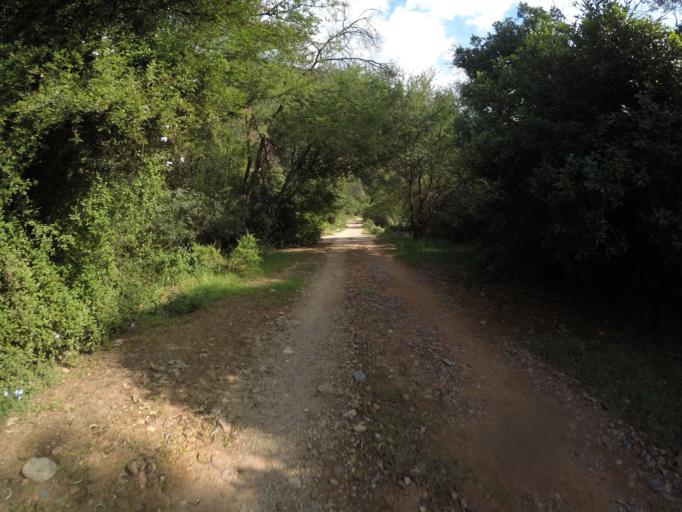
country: ZA
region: Eastern Cape
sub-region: Cacadu District Municipality
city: Kareedouw
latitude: -33.6424
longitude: 24.3169
